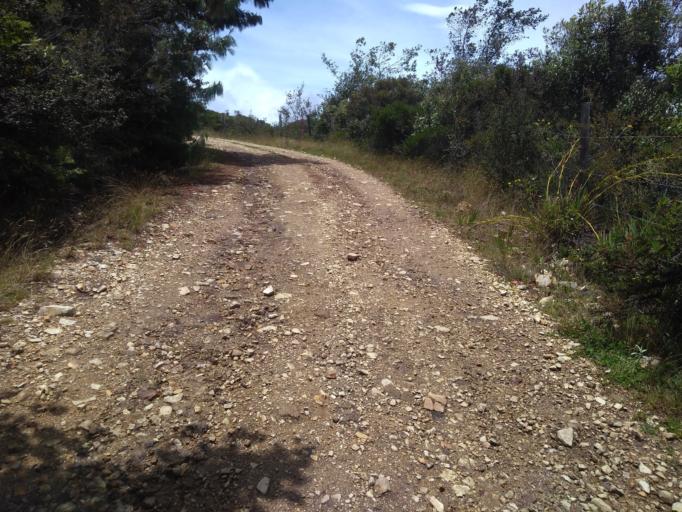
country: CO
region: Boyaca
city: Toca
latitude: 5.5874
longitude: -73.1256
